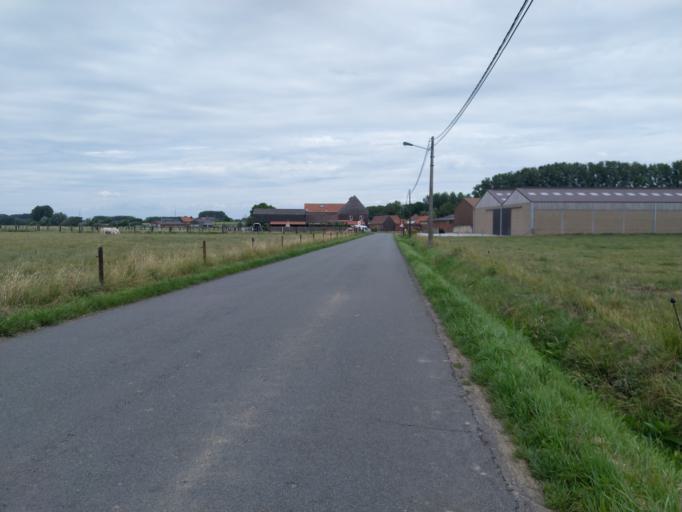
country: BE
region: Wallonia
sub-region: Province du Hainaut
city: Beloeil
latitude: 50.5478
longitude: 3.7491
